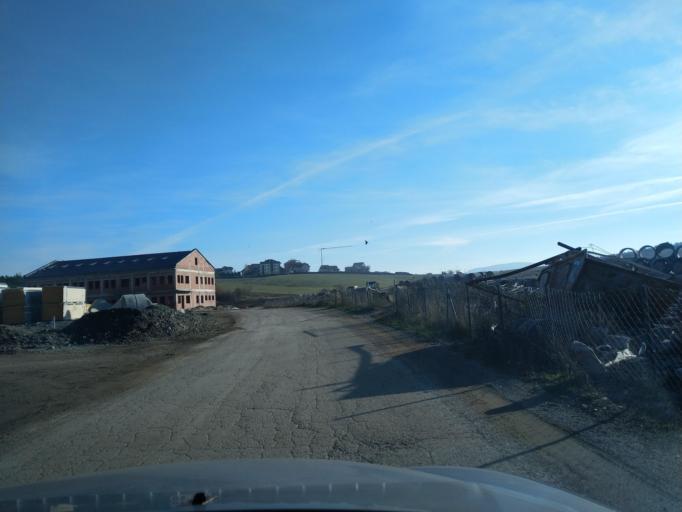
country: RS
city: Zlatibor
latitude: 43.7311
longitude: 19.6815
